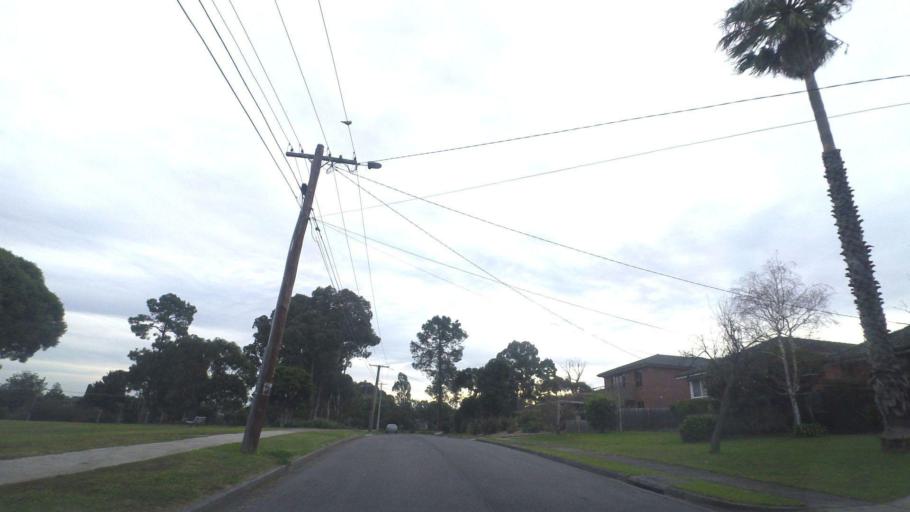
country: AU
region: Victoria
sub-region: Manningham
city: Bulleen
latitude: -37.7715
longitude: 145.0913
